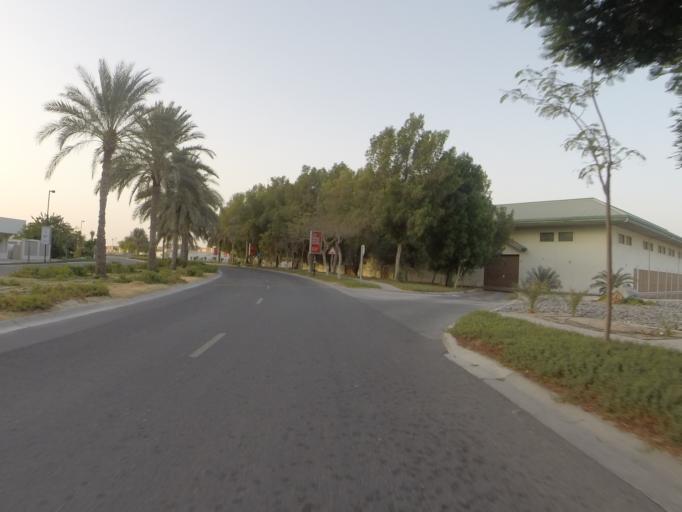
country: AE
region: Dubai
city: Dubai
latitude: 25.0622
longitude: 55.1435
